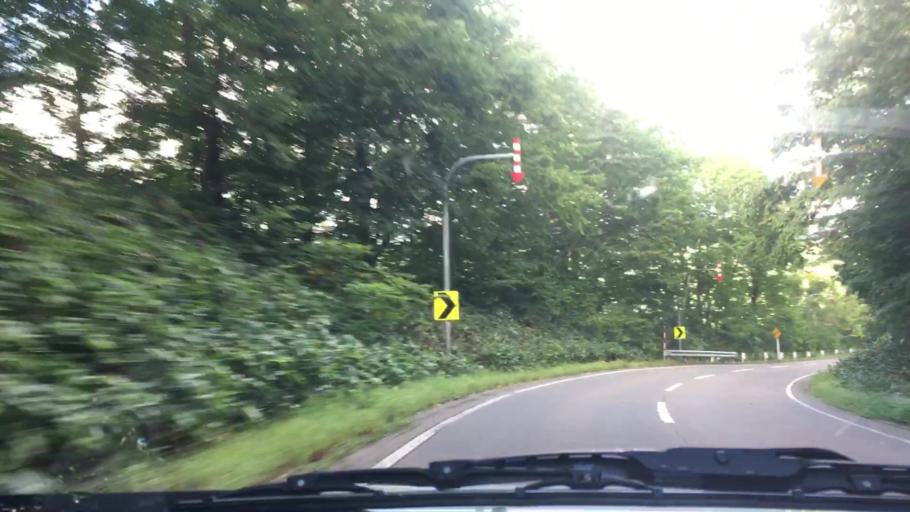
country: JP
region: Hokkaido
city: Otofuke
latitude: 43.1774
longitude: 142.9260
